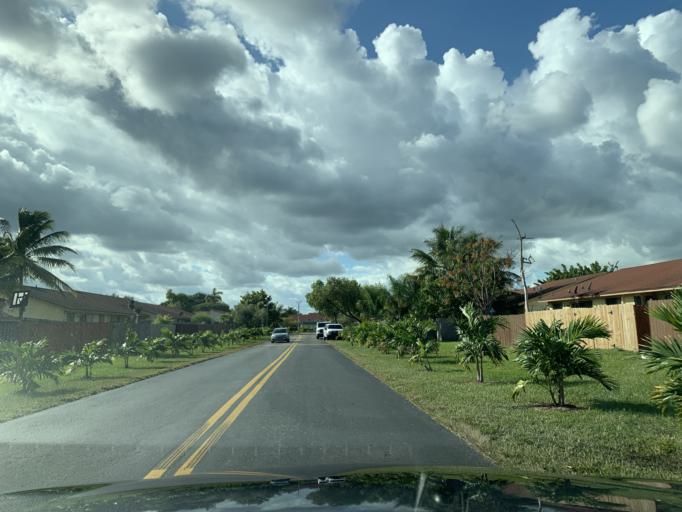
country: US
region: Florida
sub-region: Miami-Dade County
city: Naranja
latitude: 25.5061
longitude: -80.4184
